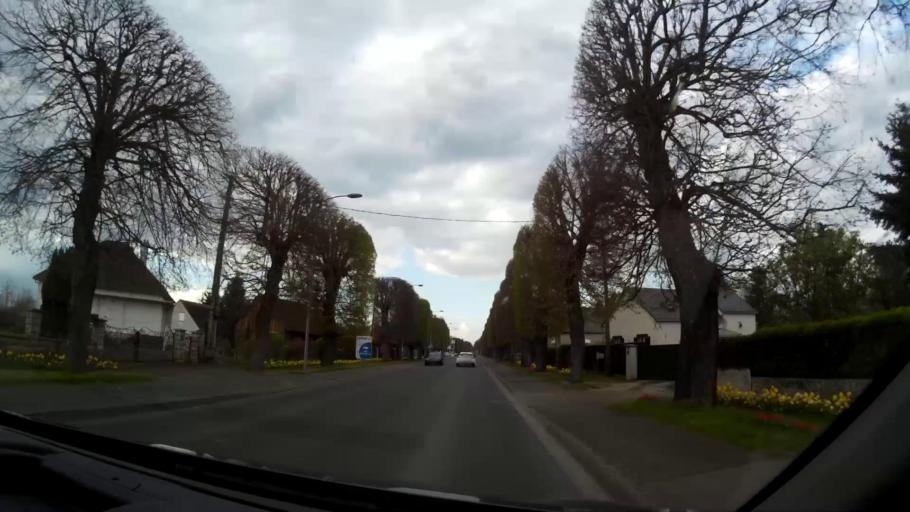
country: FR
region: Centre
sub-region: Departement du Loir-et-Cher
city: Contres
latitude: 47.4232
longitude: 1.4285
